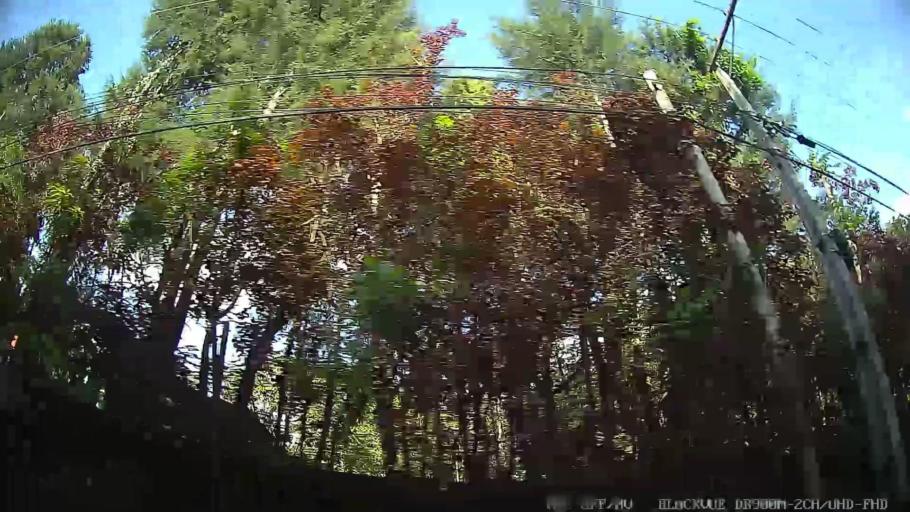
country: BR
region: Sao Paulo
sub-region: Braganca Paulista
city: Braganca Paulista
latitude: -22.9752
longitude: -46.5065
